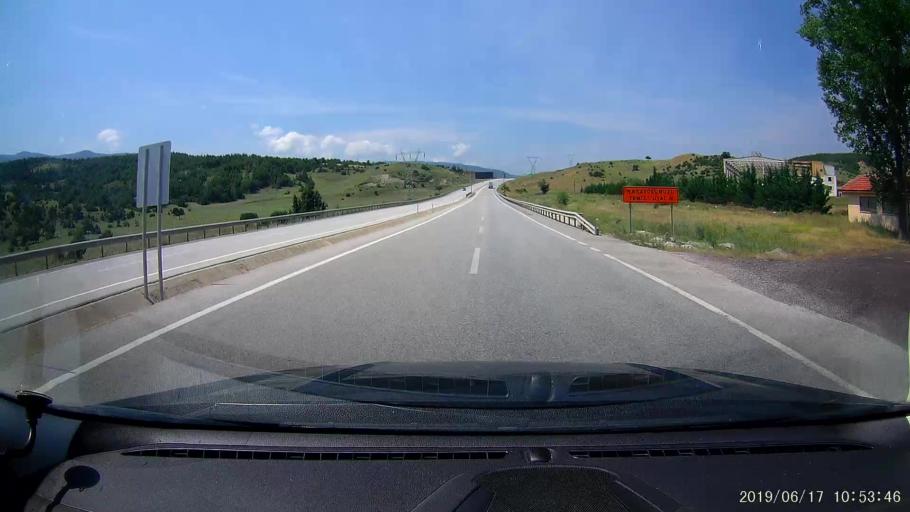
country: TR
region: Corum
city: Hacihamza
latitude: 41.0795
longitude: 34.3145
